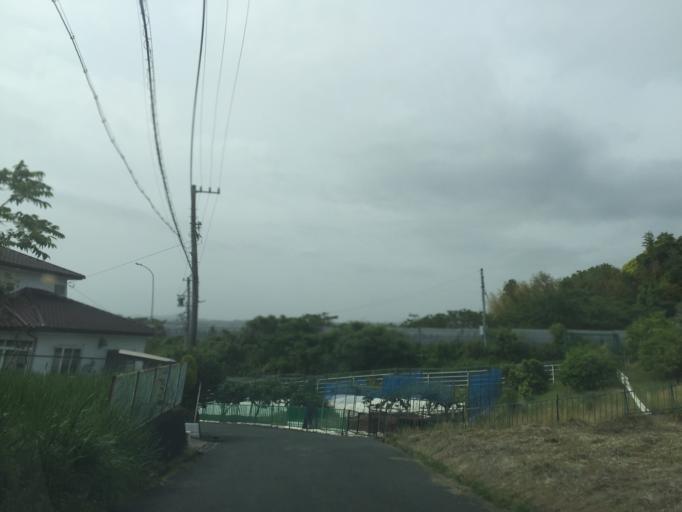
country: JP
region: Shizuoka
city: Kakegawa
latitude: 34.7877
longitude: 138.0175
